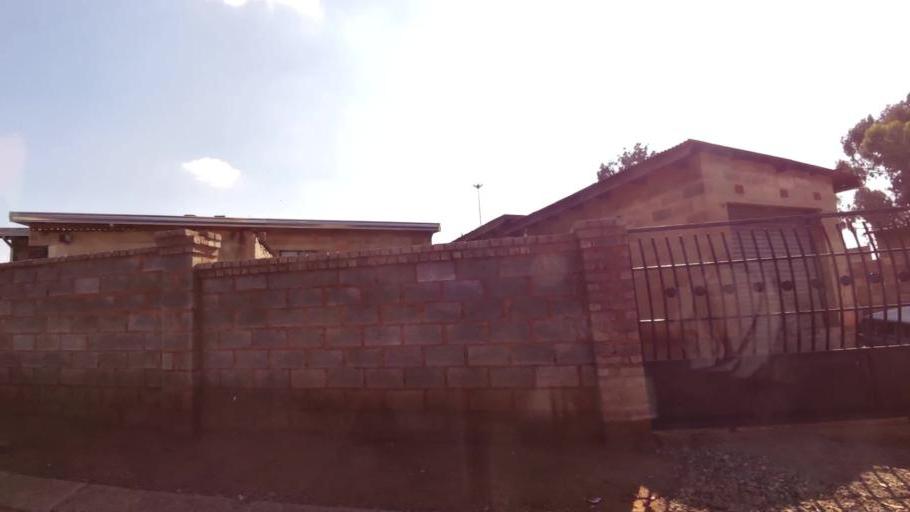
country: ZA
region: Gauteng
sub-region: City of Johannesburg Metropolitan Municipality
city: Soweto
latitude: -26.2339
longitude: 27.8861
